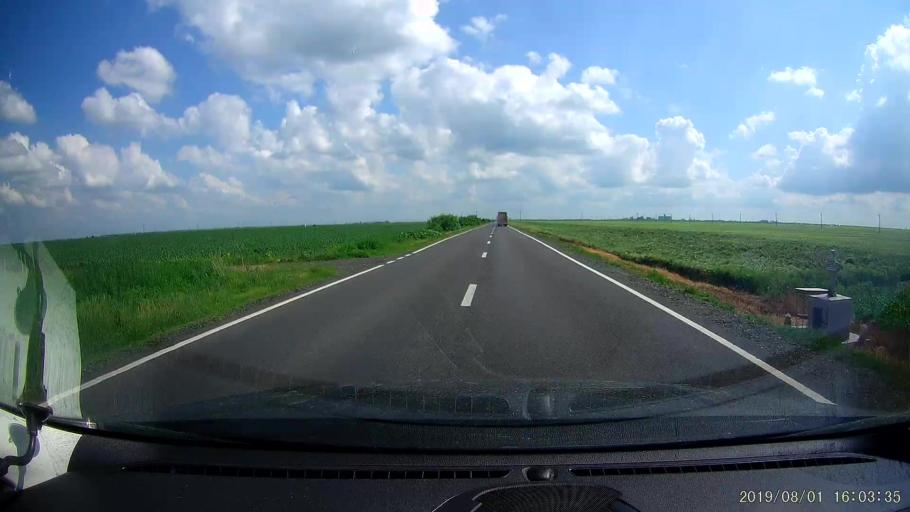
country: RO
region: Calarasi
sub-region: Comuna Dragalina
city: Drajna Noua
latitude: 44.4686
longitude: 27.3838
